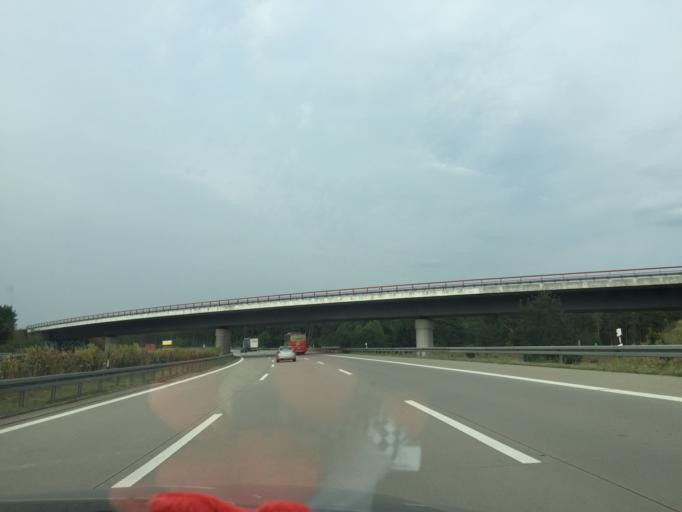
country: DE
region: Brandenburg
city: Erkner
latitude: 52.3259
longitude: 13.7474
